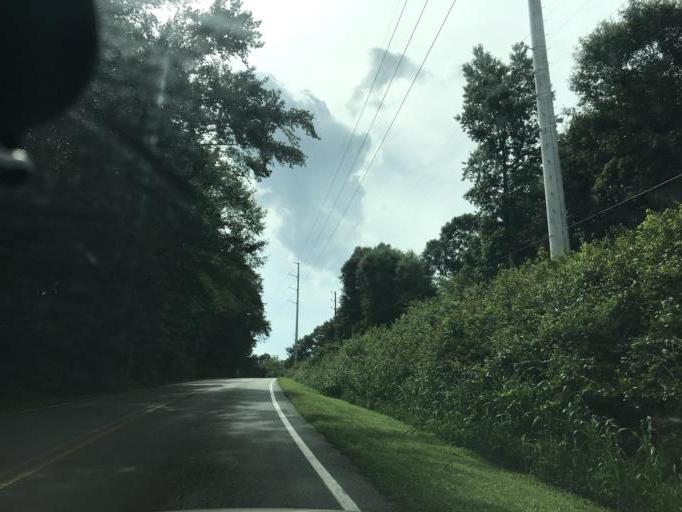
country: US
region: Georgia
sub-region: Forsyth County
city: Cumming
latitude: 34.3110
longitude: -84.2304
